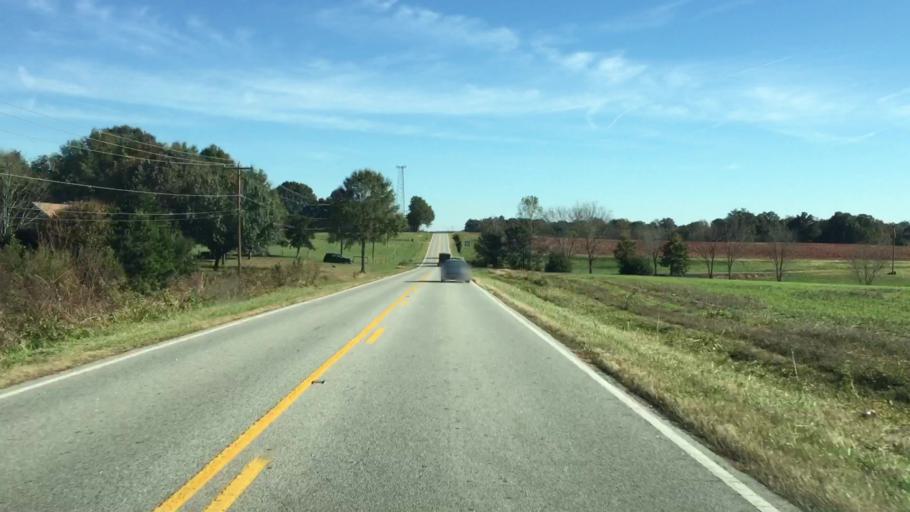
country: US
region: North Carolina
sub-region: Rowan County
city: Enochville
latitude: 35.6281
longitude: -80.6812
